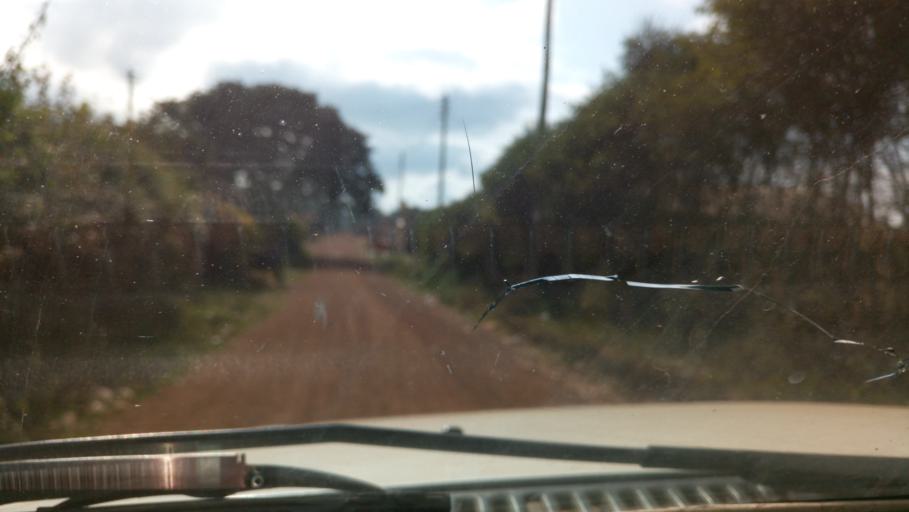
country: KE
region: Nairobi Area
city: Thika
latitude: -0.9236
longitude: 37.1302
